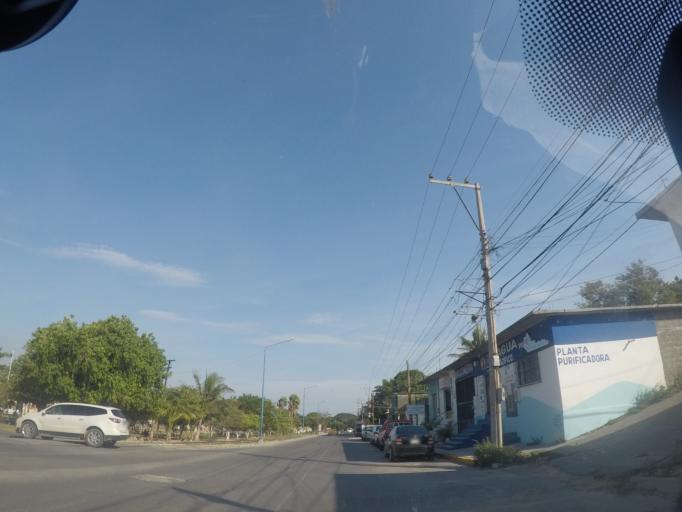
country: MX
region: Oaxaca
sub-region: Salina Cruz
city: Salina Cruz
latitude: 16.1851
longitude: -95.2005
